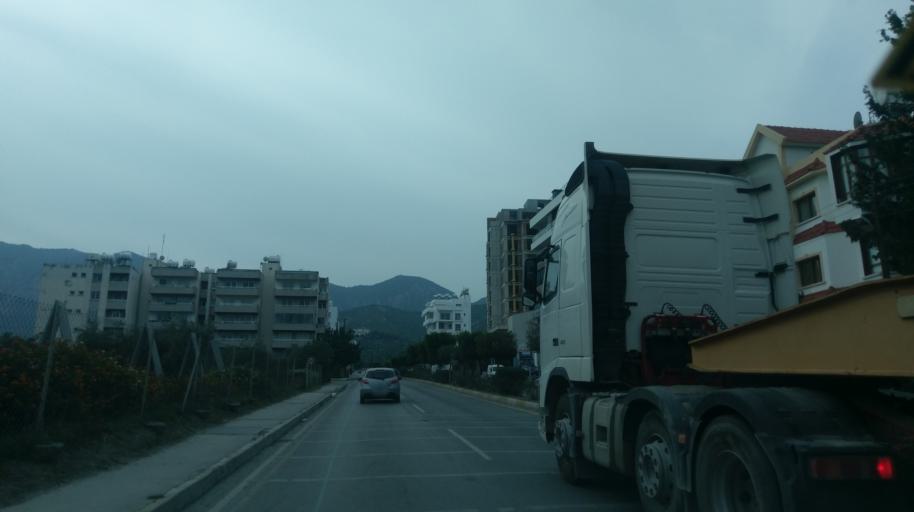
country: CY
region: Keryneia
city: Kyrenia
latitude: 35.3297
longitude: 33.3192
